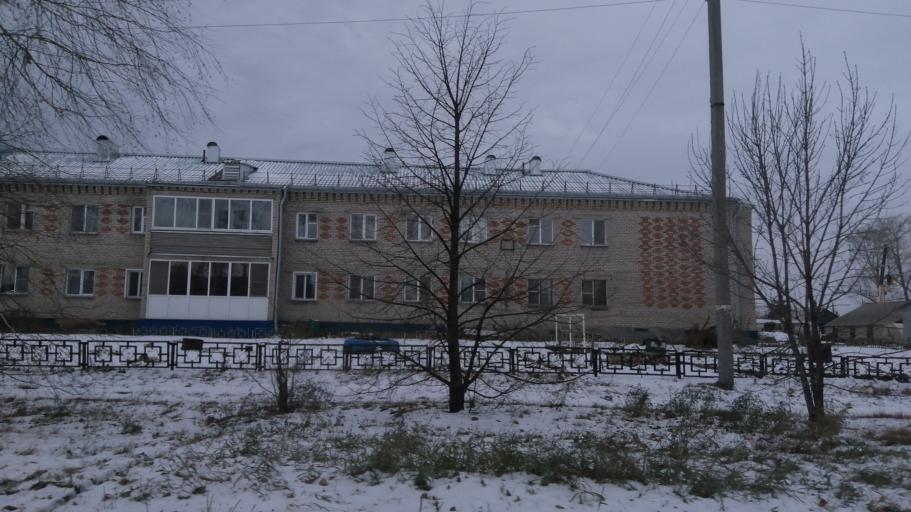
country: RU
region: Novosibirsk
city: Krasnozerskoye
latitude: 53.9802
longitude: 79.2414
